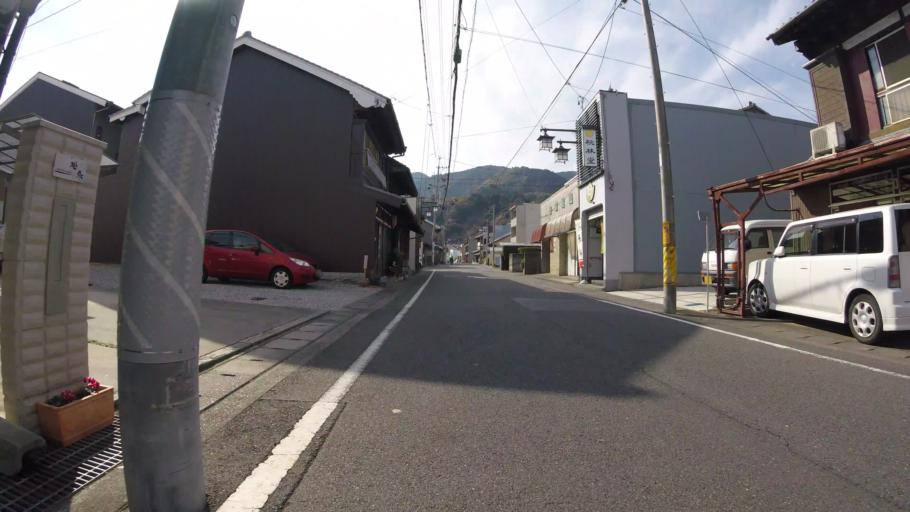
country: JP
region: Shizuoka
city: Fujinomiya
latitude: 35.1034
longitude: 138.5583
